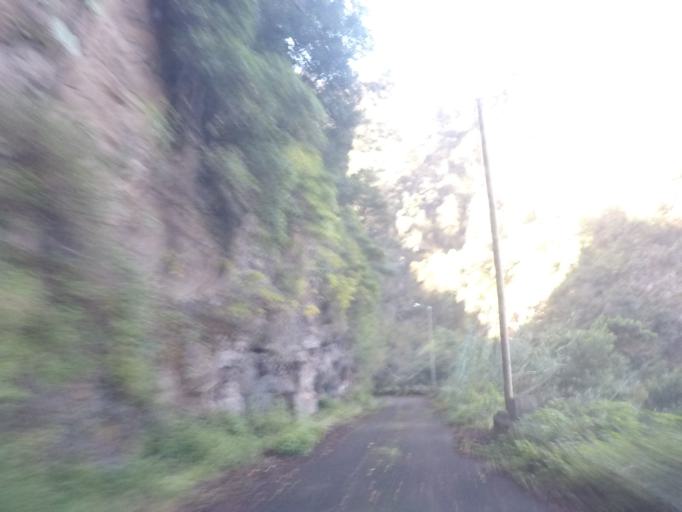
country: PT
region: Madeira
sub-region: Santana
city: Santana
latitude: 32.8160
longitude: -16.8938
